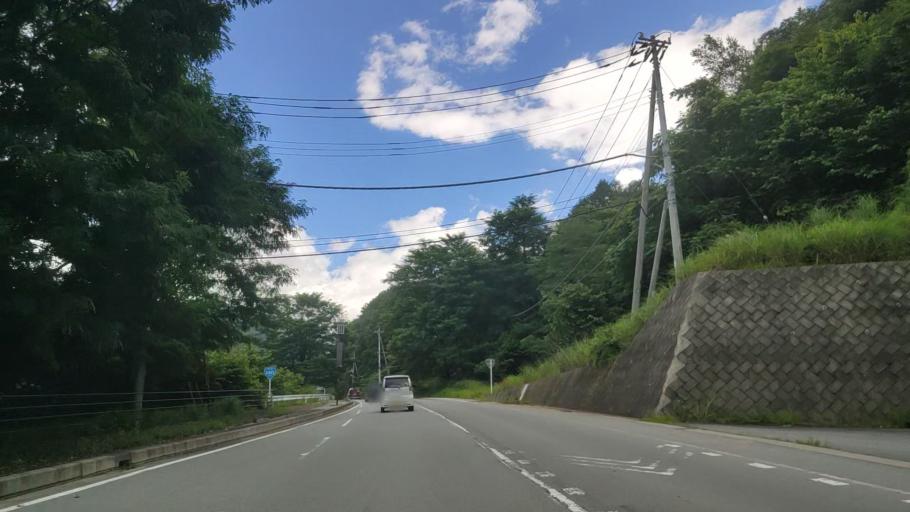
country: JP
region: Yamanashi
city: Enzan
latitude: 35.8041
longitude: 138.7505
